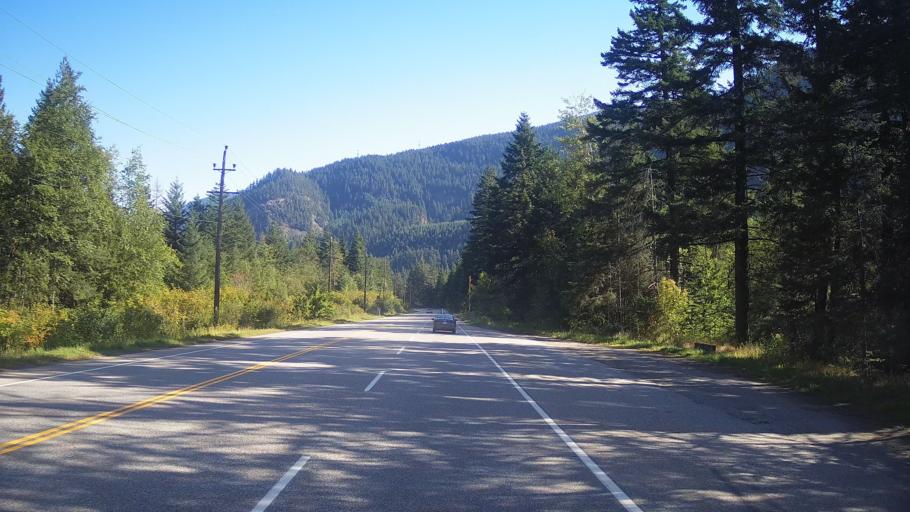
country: CA
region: British Columbia
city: Hope
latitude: 49.6493
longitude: -121.4083
